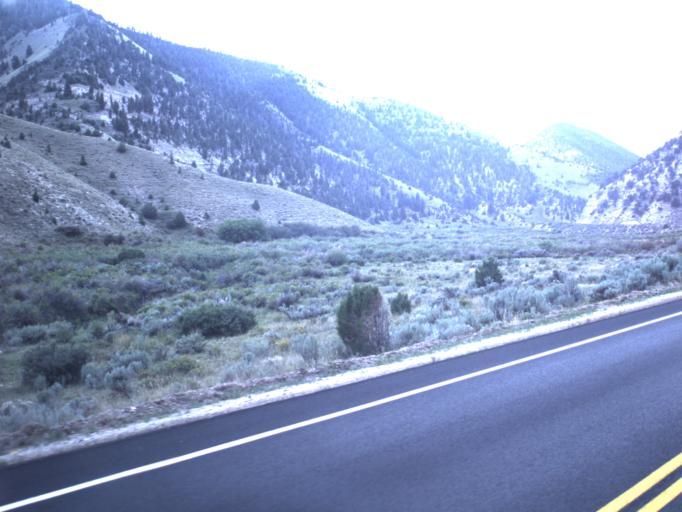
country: US
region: Utah
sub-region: Duchesne County
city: Duchesne
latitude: 39.9819
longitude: -110.6145
